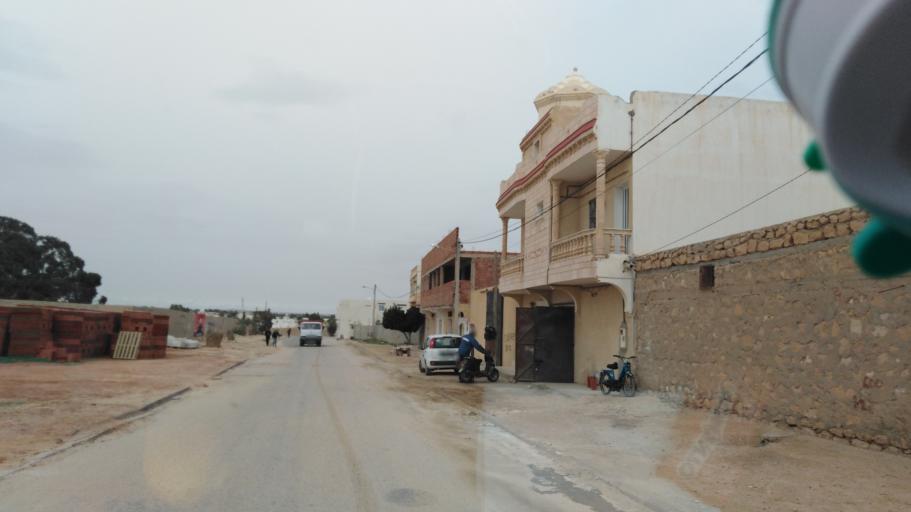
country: TN
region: Qabis
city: Gabes
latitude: 33.9539
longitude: 10.0033
